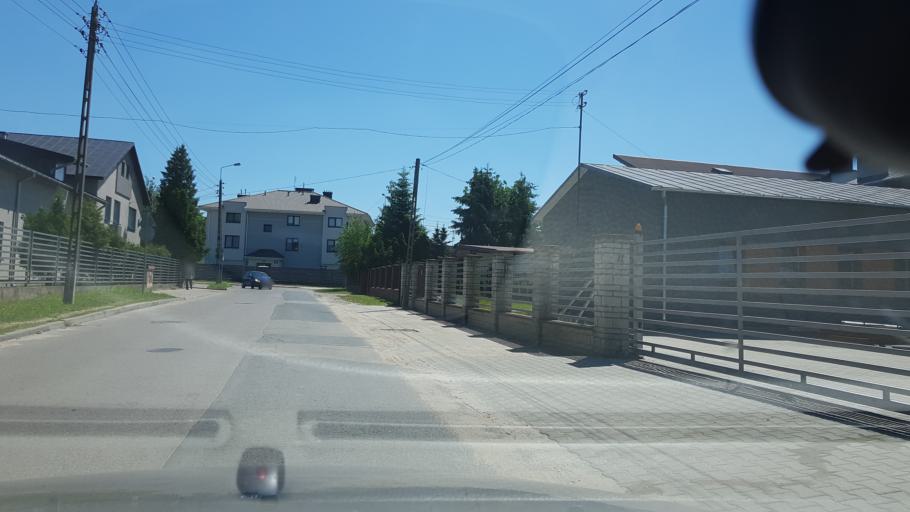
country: PL
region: Masovian Voivodeship
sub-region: Powiat wolominski
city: Marki
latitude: 52.3116
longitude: 21.1078
